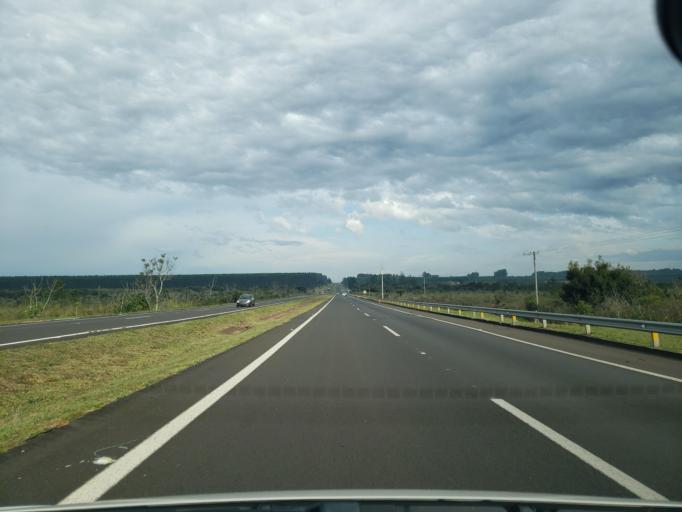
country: BR
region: Sao Paulo
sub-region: Itirapina
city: Itirapina
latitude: -22.2572
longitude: -47.8590
